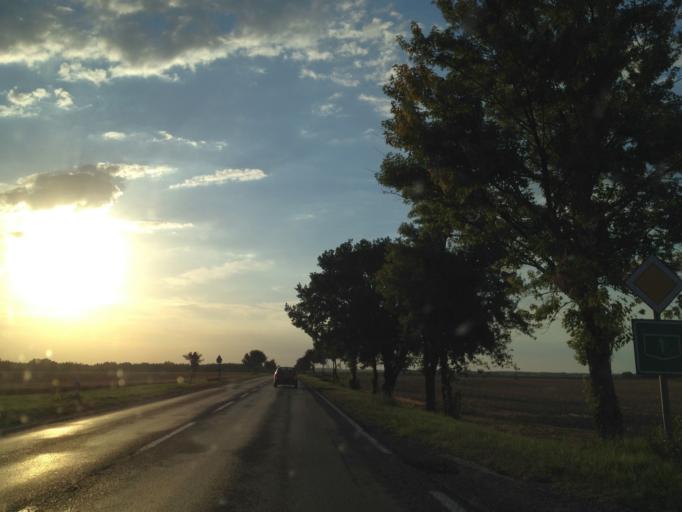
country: HU
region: Gyor-Moson-Sopron
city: Kimle
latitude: 47.7858
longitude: 17.4088
